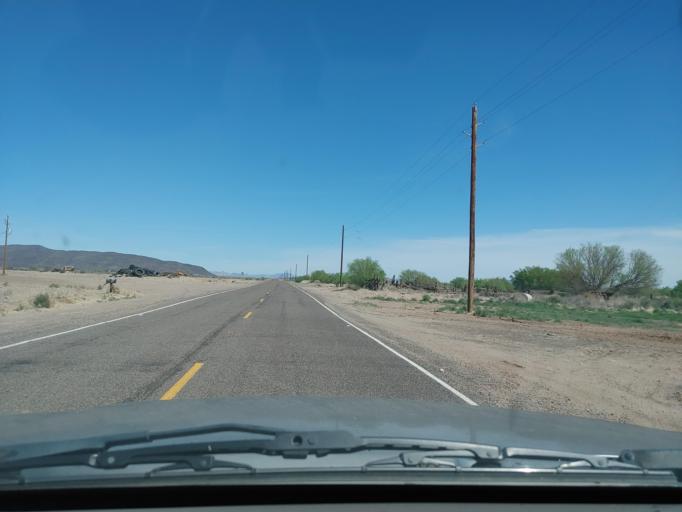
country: US
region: Arizona
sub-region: Maricopa County
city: Gila Bend
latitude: 32.9563
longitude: -113.3058
